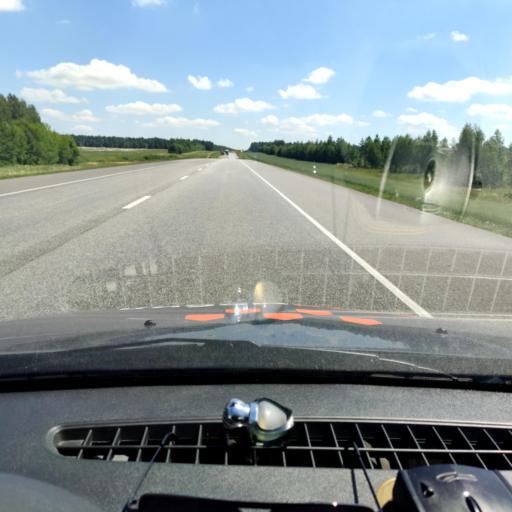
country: RU
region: Orjol
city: Zmiyevka
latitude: 52.8112
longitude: 36.2904
